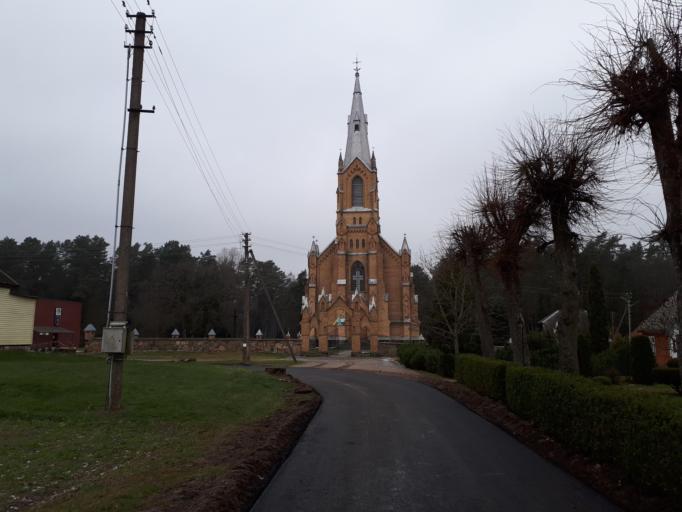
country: LT
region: Alytaus apskritis
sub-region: Alytus
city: Alytus
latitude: 54.3022
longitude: 24.0206
